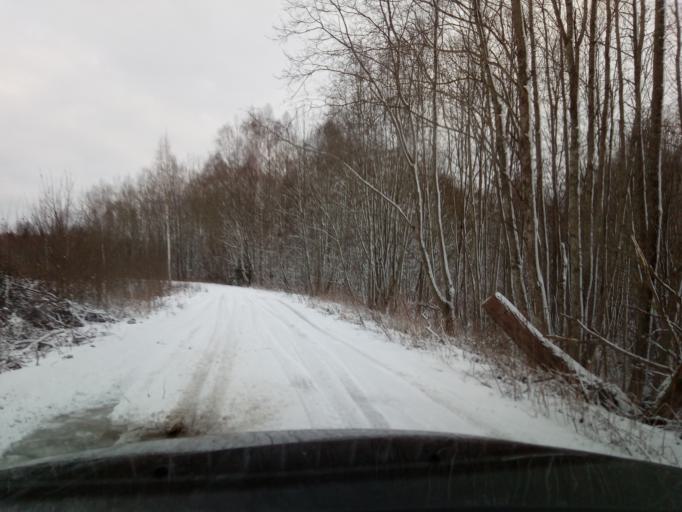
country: LT
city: Zarasai
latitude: 55.7325
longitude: 25.9425
